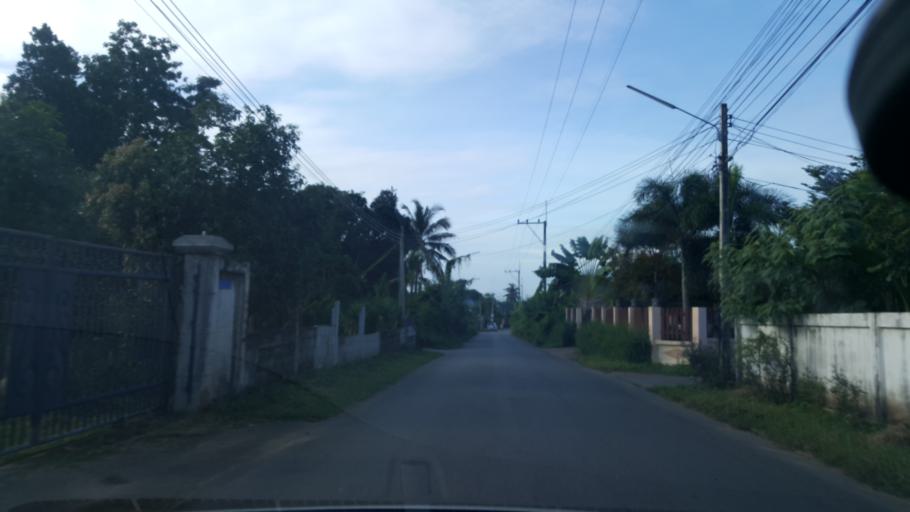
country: TH
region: Chon Buri
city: Sattahip
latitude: 12.6799
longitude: 100.9107
